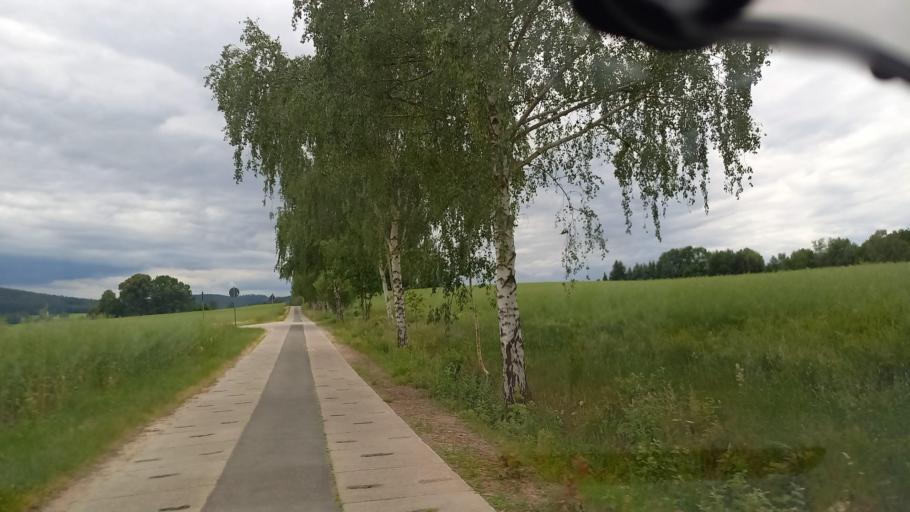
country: DE
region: Saxony
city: Kirchberg
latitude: 50.6009
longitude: 12.5405
